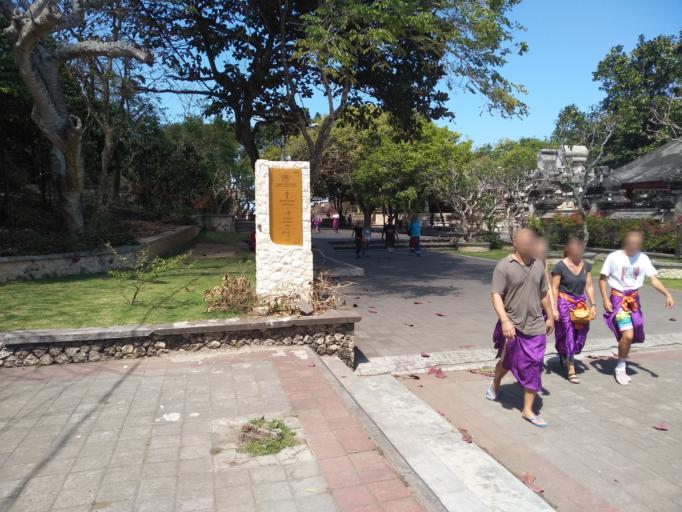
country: ID
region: Bali
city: Pecatu
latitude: -8.8290
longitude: 115.0855
